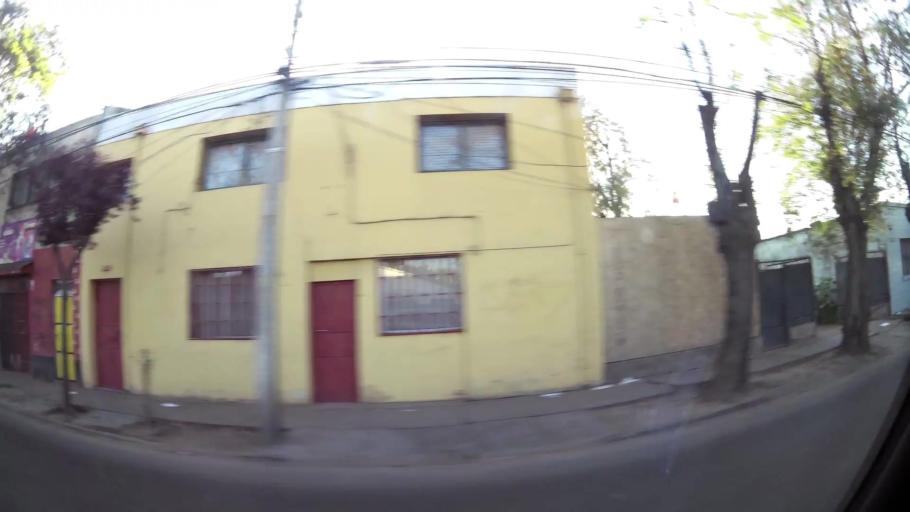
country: CL
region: Santiago Metropolitan
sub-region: Provincia de Santiago
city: Lo Prado
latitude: -33.4234
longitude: -70.7184
